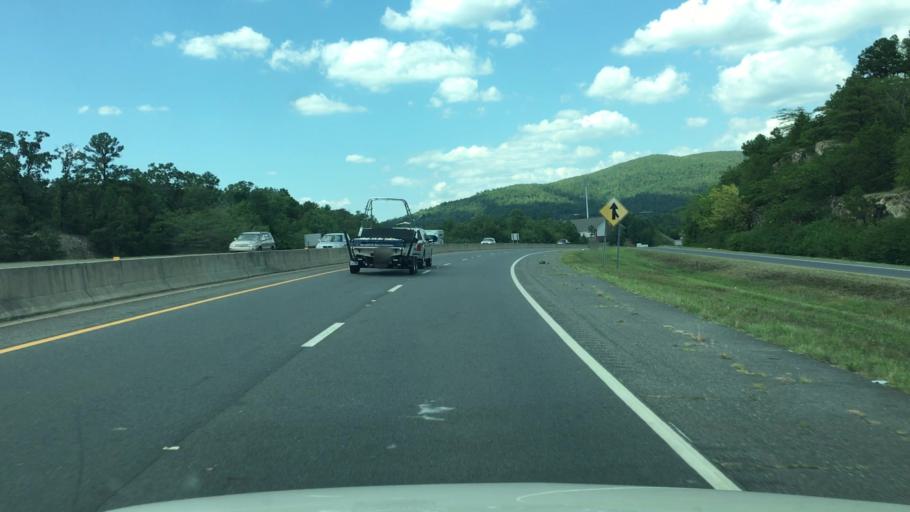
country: US
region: Arkansas
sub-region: Garland County
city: Rockwell
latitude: 34.4794
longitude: -93.1149
